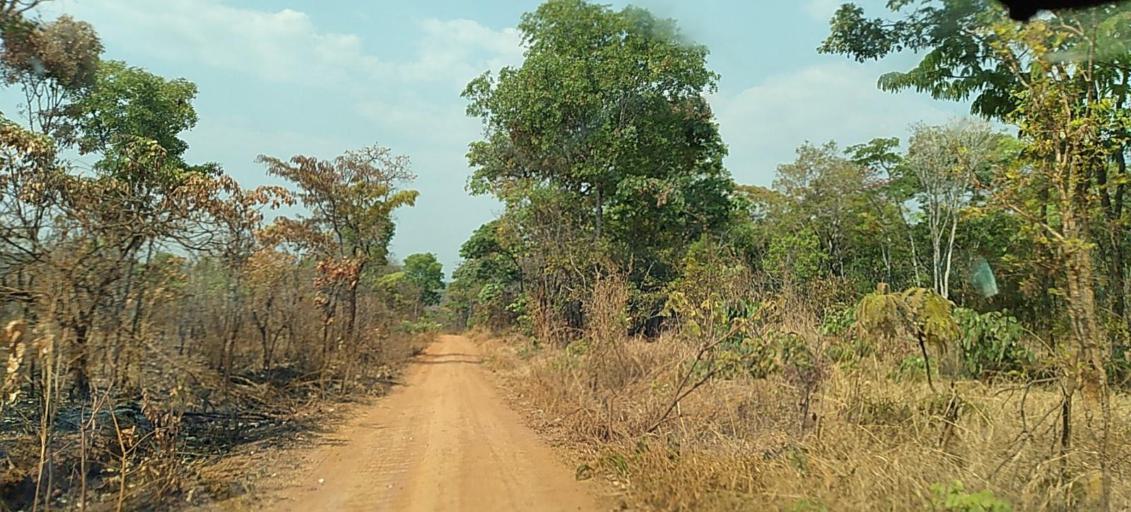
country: ZM
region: North-Western
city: Kasempa
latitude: -13.3106
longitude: 26.0634
